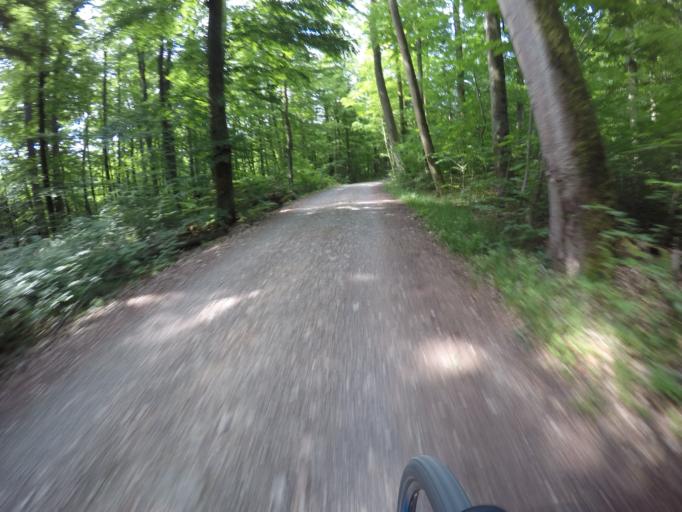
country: DE
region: Baden-Wuerttemberg
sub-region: Regierungsbezirk Stuttgart
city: Denkendorf
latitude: 48.6731
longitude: 9.3161
